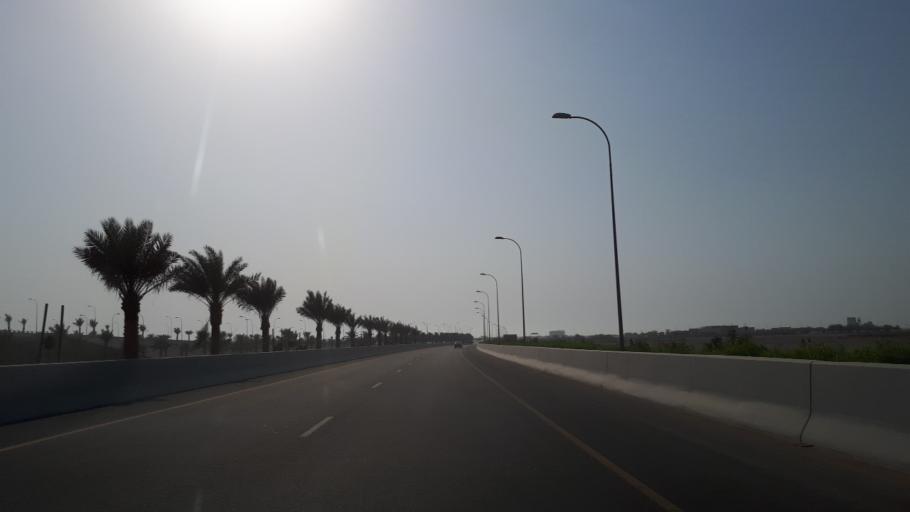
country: OM
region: Muhafazat Masqat
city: Bawshar
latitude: 23.5982
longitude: 58.3312
